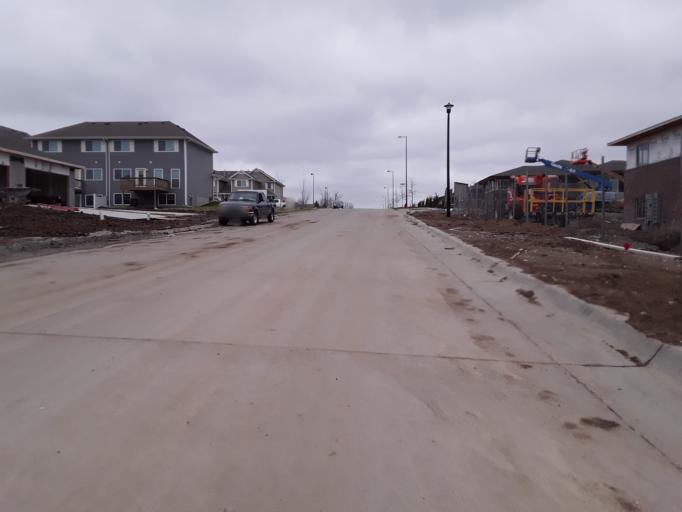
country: US
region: Nebraska
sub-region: Lancaster County
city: Lincoln
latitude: 40.8499
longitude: -96.5991
